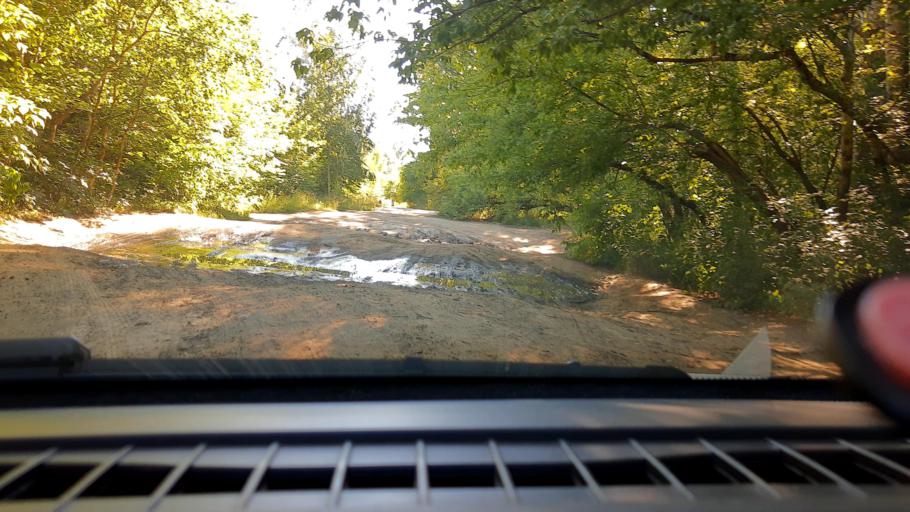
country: RU
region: Nizjnij Novgorod
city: Burevestnik
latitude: 56.1993
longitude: 43.8229
